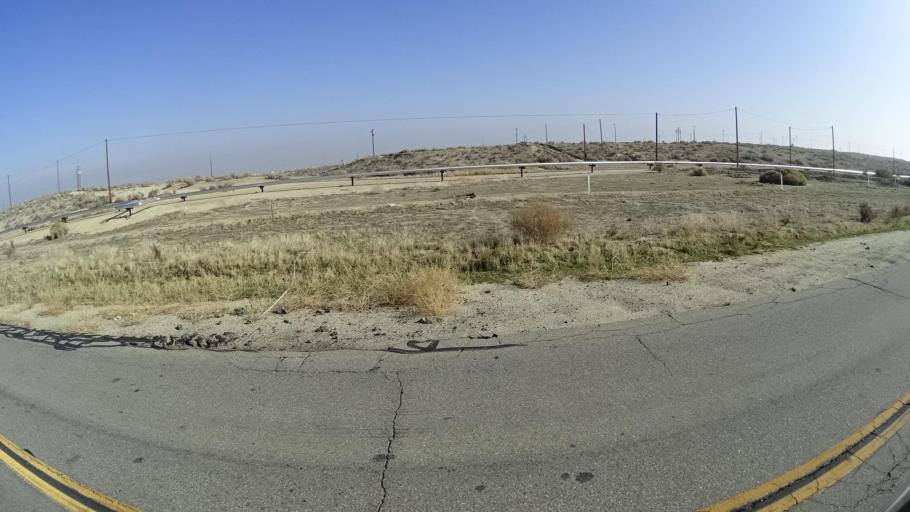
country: US
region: California
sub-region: Kern County
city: Taft Heights
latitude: 35.1699
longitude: -119.5340
